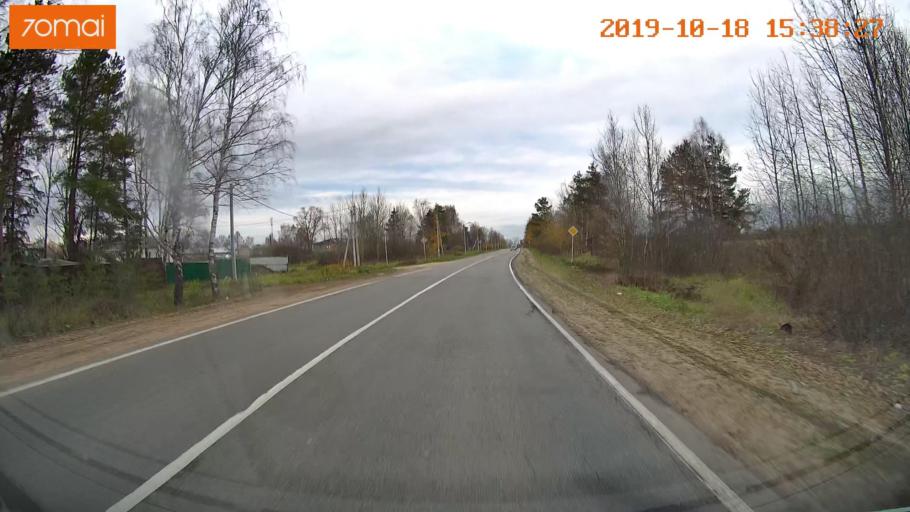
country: RU
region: Vladimir
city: Golovino
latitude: 55.9112
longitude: 40.6071
